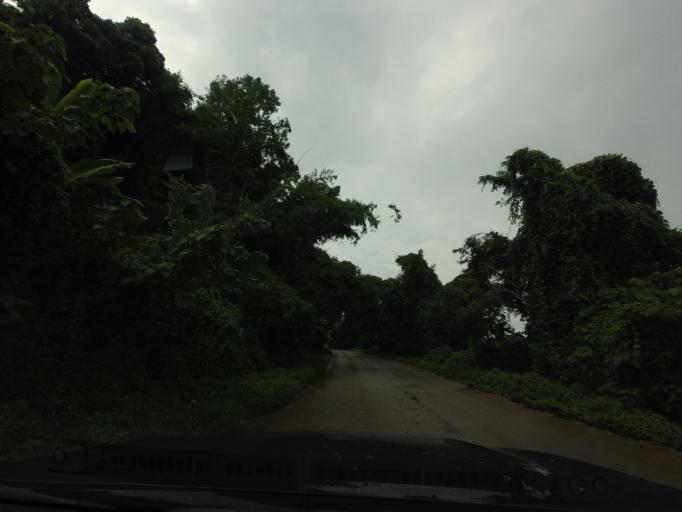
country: TH
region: Loei
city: Pak Chom
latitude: 18.1141
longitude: 101.9885
